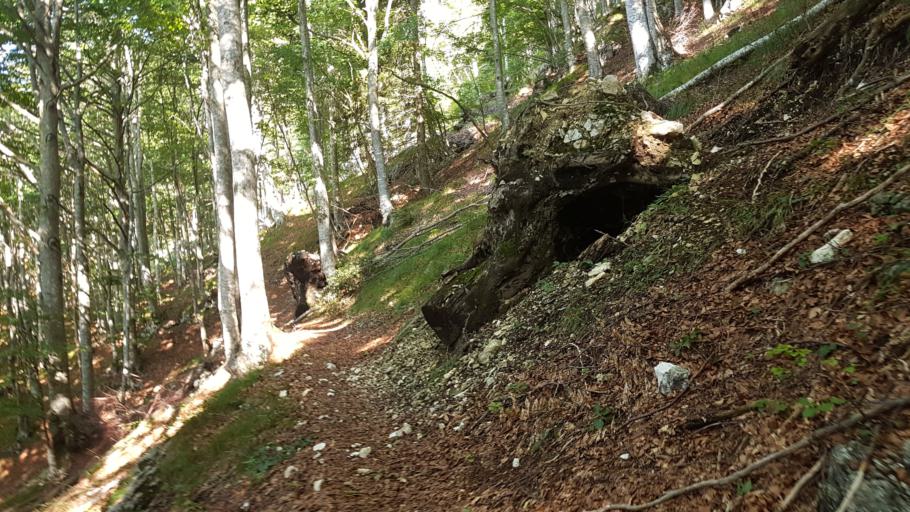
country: IT
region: Friuli Venezia Giulia
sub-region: Provincia di Udine
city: Moggio Udinese
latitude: 46.4631
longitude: 13.2177
